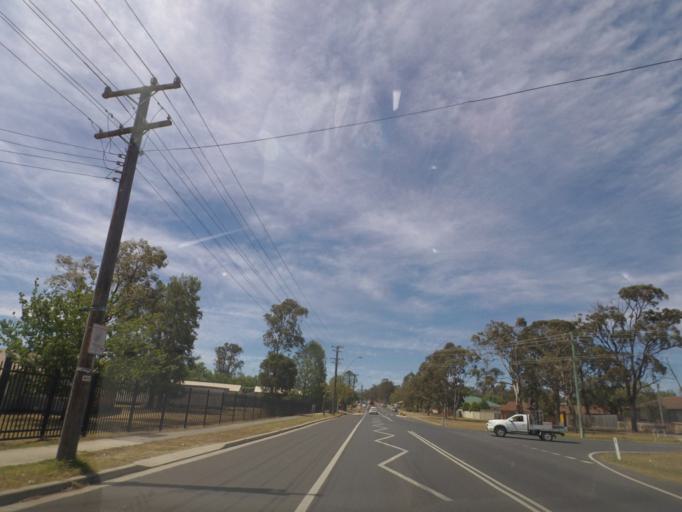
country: AU
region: New South Wales
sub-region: Wollondilly
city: Picton
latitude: -34.2282
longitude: 150.5897
